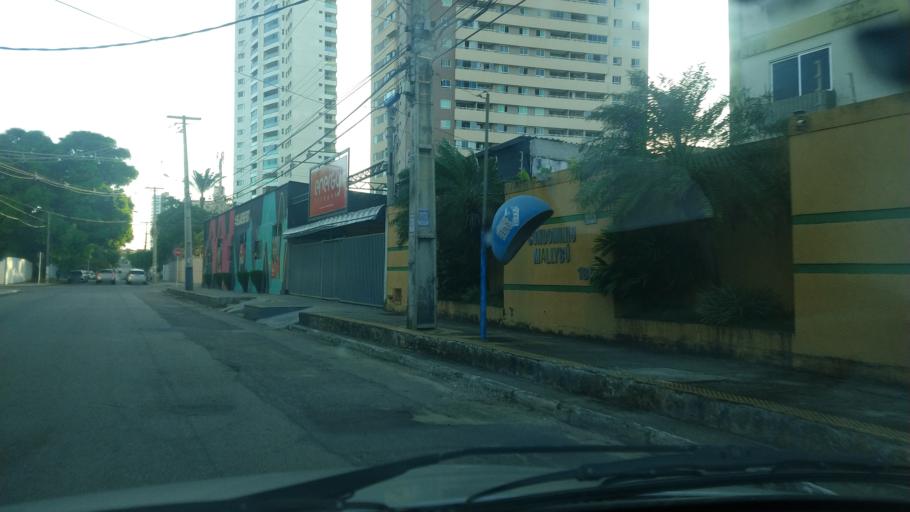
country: BR
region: Rio Grande do Norte
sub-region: Natal
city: Natal
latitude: -5.8588
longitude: -35.1973
